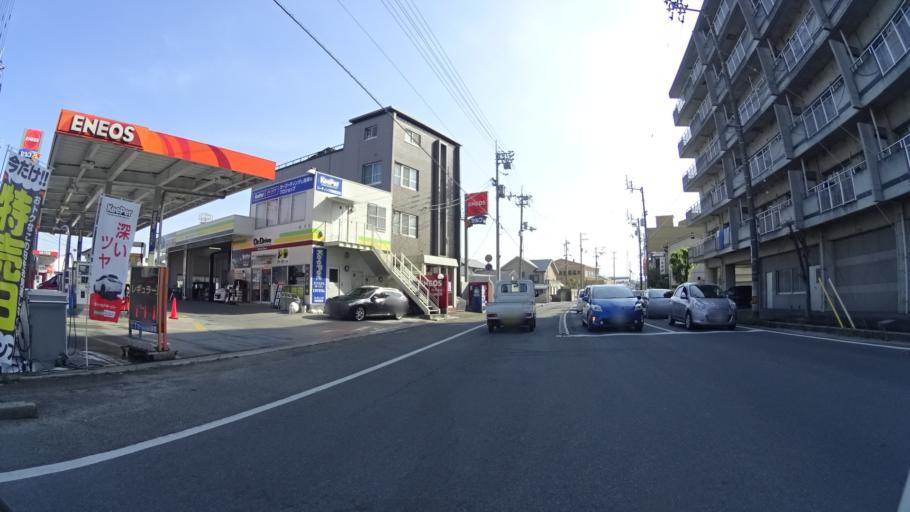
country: JP
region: Ehime
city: Saijo
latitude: 34.0605
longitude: 133.0114
